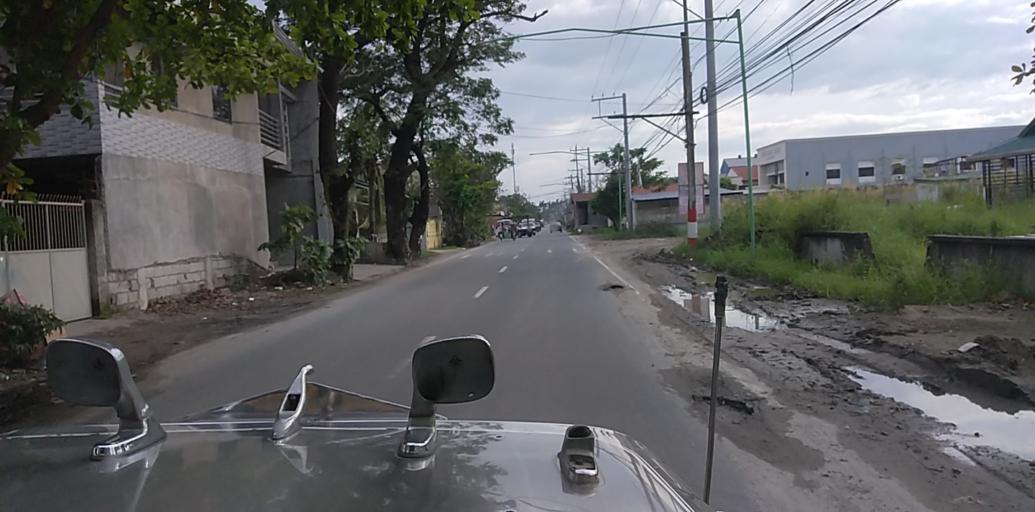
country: PH
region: Central Luzon
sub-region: Province of Pampanga
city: Minalin
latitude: 14.9926
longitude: 120.7043
